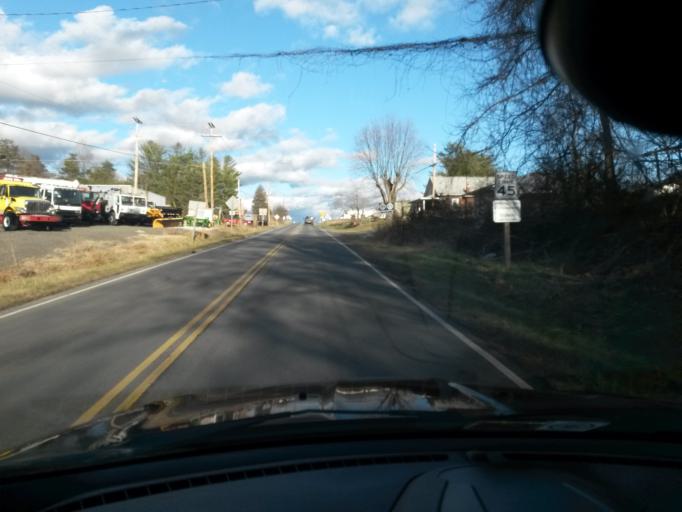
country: US
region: Virginia
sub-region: Giles County
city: Narrows
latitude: 37.3892
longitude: -80.8112
